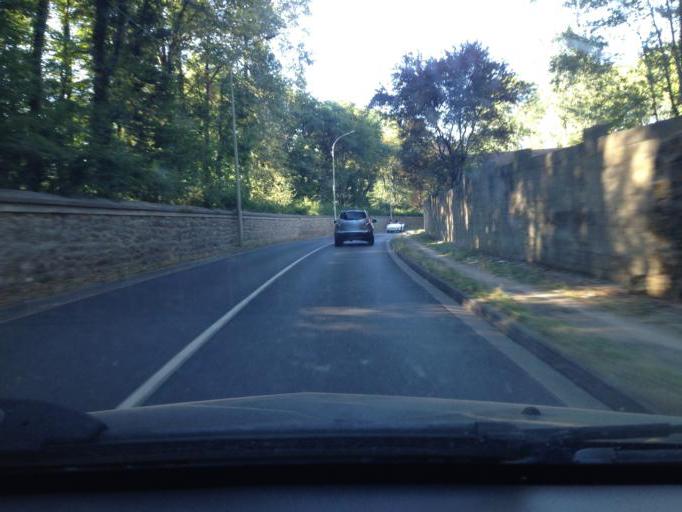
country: FR
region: Ile-de-France
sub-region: Departement des Yvelines
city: Saint-Remy-les-Chevreuse
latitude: 48.7115
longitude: 2.0845
